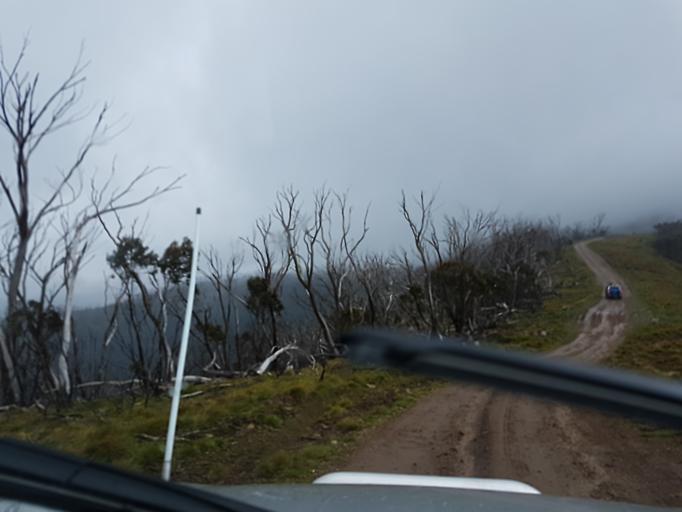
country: AU
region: Victoria
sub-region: Alpine
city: Mount Beauty
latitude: -37.0881
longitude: 147.1037
